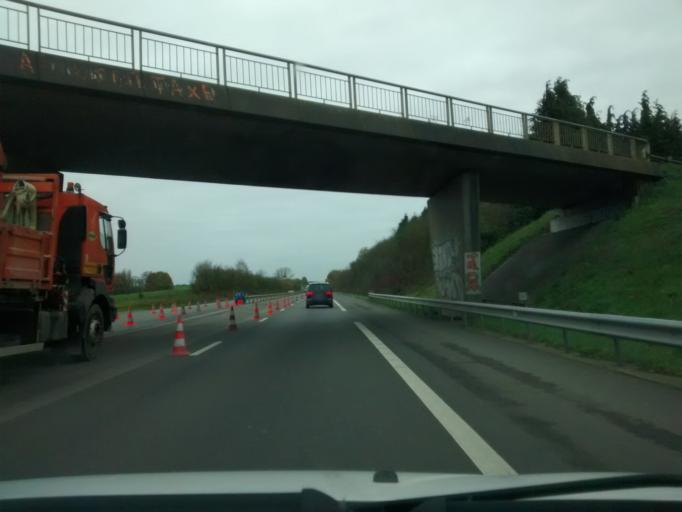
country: FR
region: Brittany
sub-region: Departement d'Ille-et-Vilaine
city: Saint-Didier
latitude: 48.0883
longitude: -1.3606
